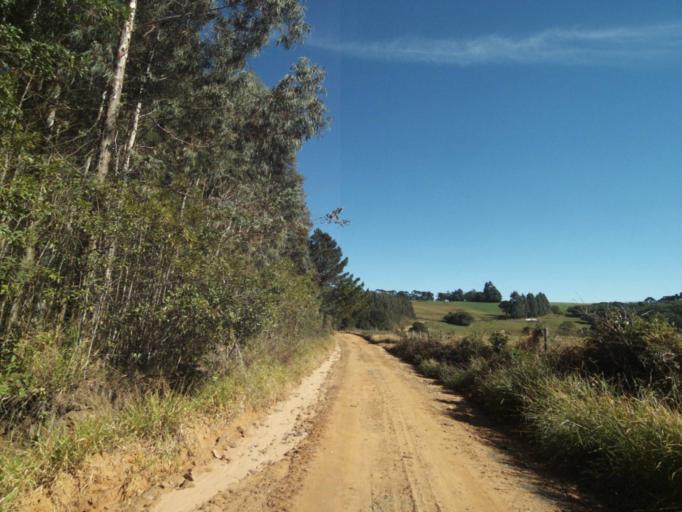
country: BR
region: Parana
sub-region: Tibagi
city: Tibagi
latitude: -24.5908
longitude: -50.2583
